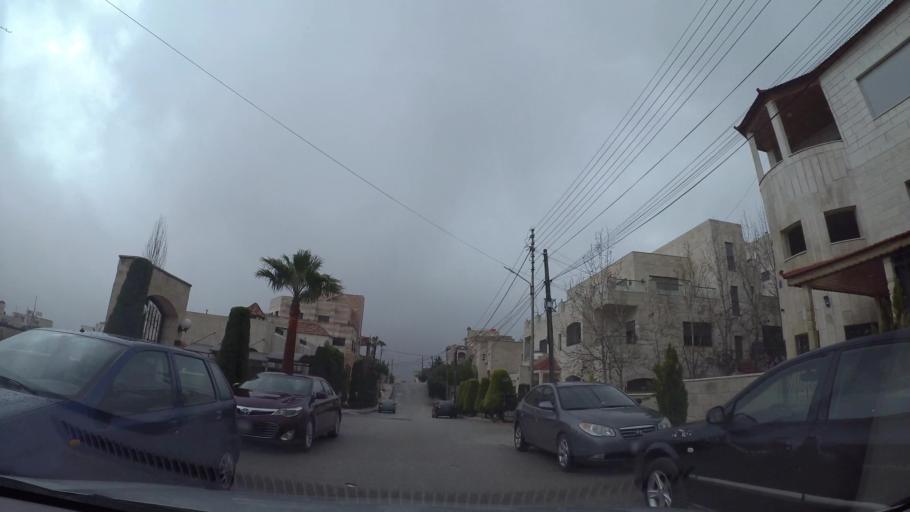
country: JO
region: Amman
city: Al Jubayhah
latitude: 32.0149
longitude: 35.8302
